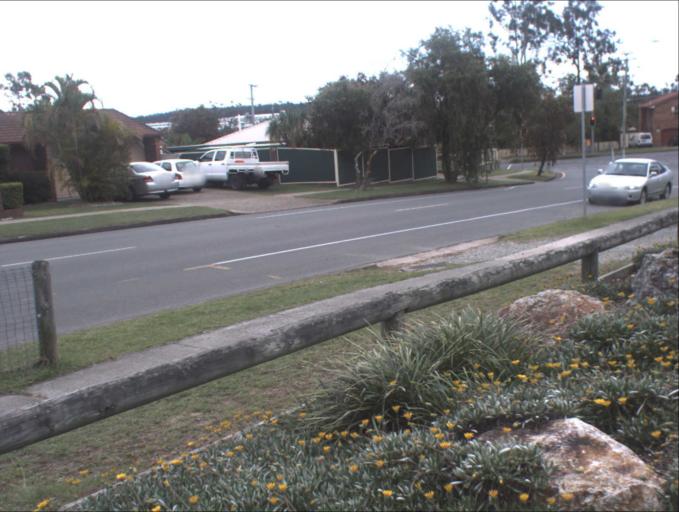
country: AU
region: Queensland
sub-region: Brisbane
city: Sunnybank Hills
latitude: -27.6679
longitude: 153.0393
